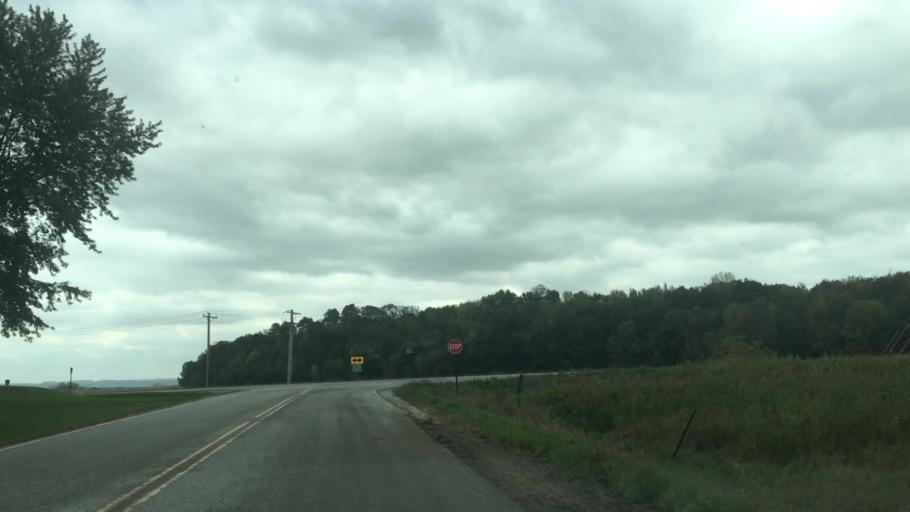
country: US
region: Minnesota
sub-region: Fillmore County
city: Preston
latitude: 43.7344
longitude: -92.0055
